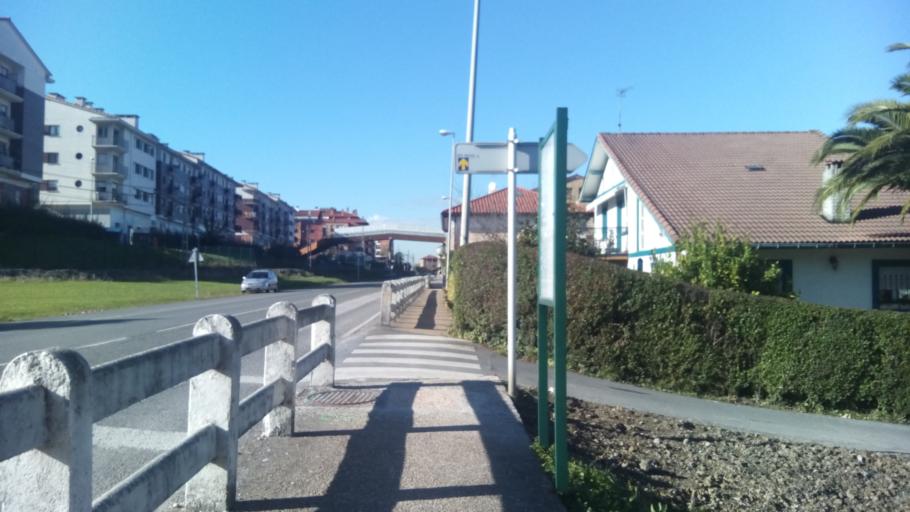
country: ES
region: Basque Country
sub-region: Bizkaia
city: Zamudio
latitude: 43.2825
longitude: -2.8592
